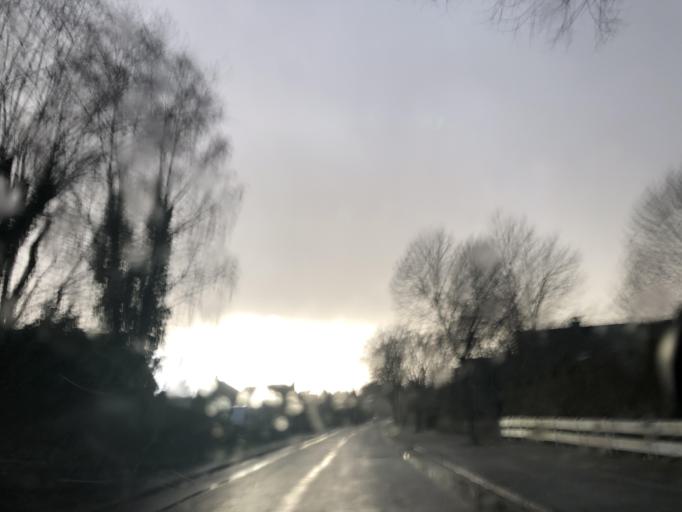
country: DE
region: Lower Saxony
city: Bad Fallingbostel
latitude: 52.8749
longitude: 9.7003
